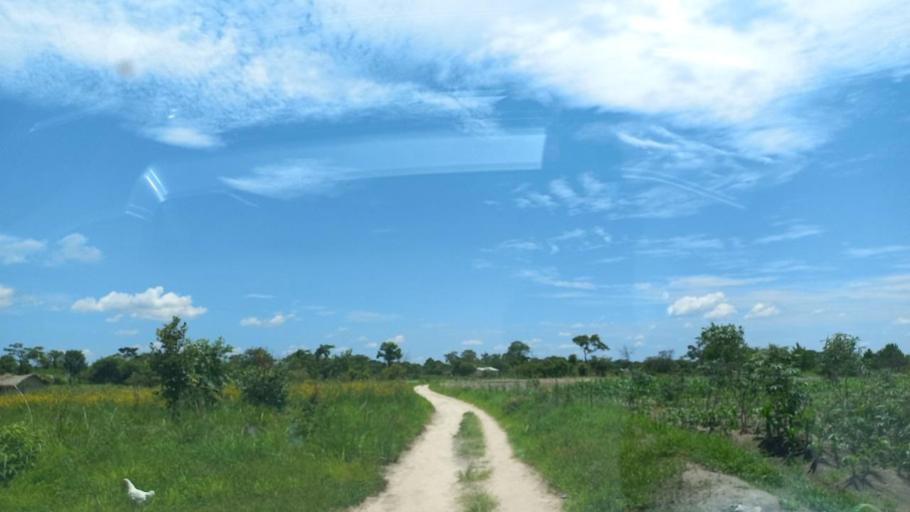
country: ZM
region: Copperbelt
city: Ndola
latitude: -12.8700
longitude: 28.4433
